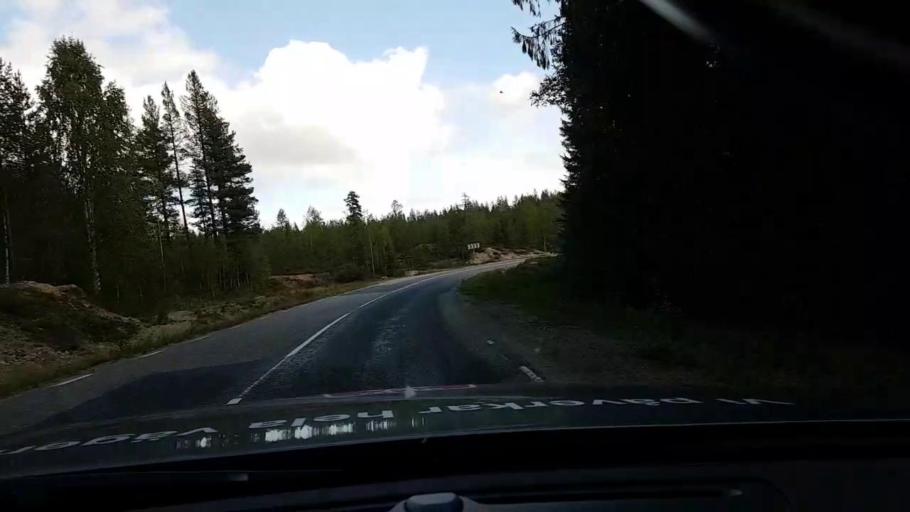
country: SE
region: Vaesterbotten
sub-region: Asele Kommun
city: Asele
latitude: 63.8058
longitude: 17.5447
